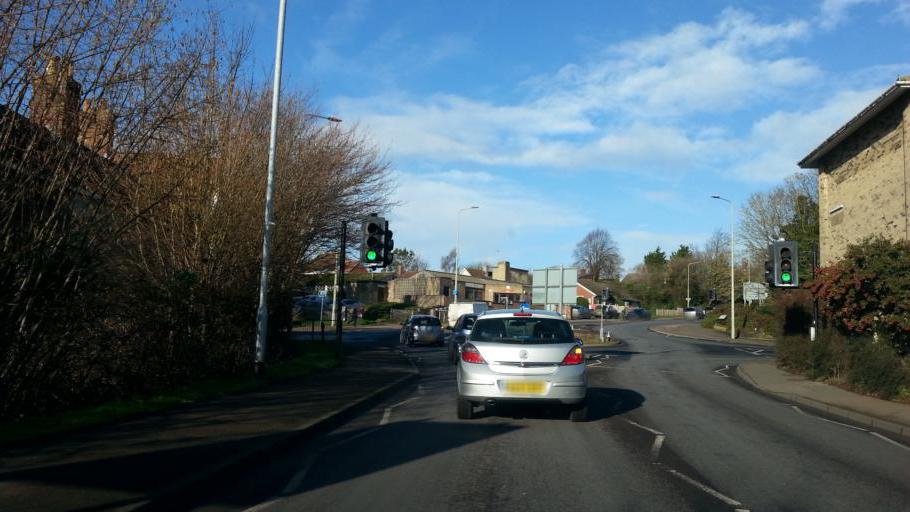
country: GB
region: England
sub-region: Suffolk
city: Halesworth
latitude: 52.3450
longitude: 1.5030
